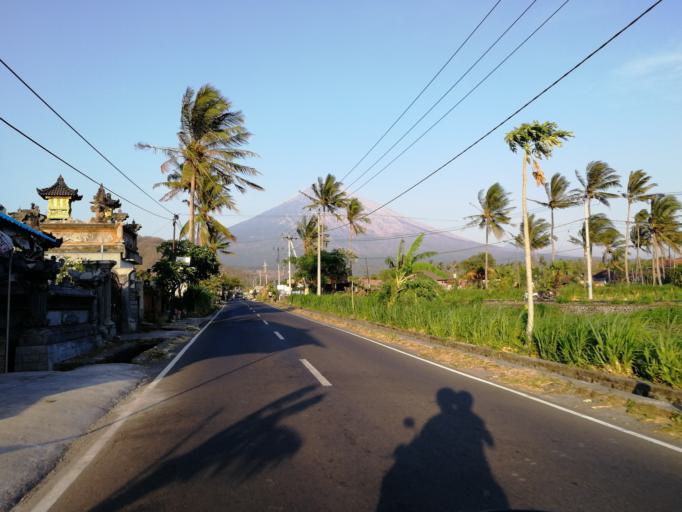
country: ID
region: Bali
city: Biaslantang Kaler
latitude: -8.3357
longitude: 115.6322
